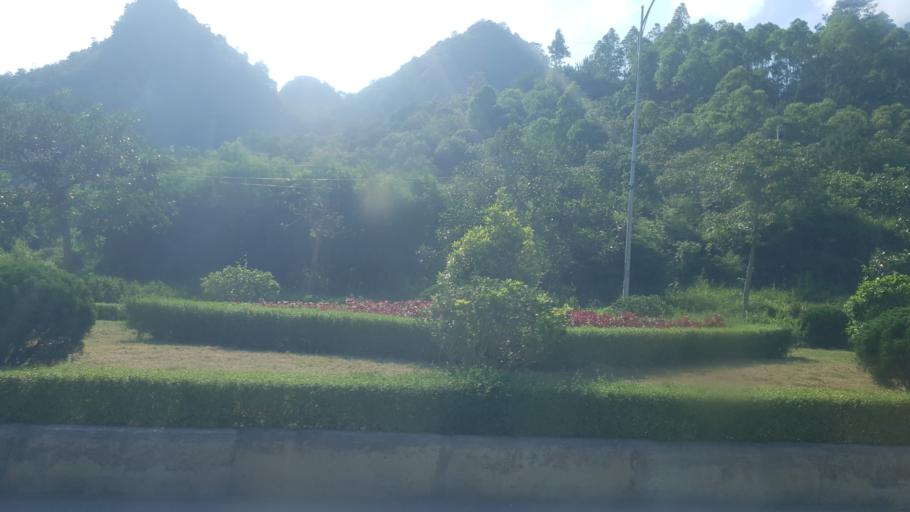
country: VN
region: Lang Son
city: Thi Tran Cao Loc
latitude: 21.9607
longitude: 106.7063
